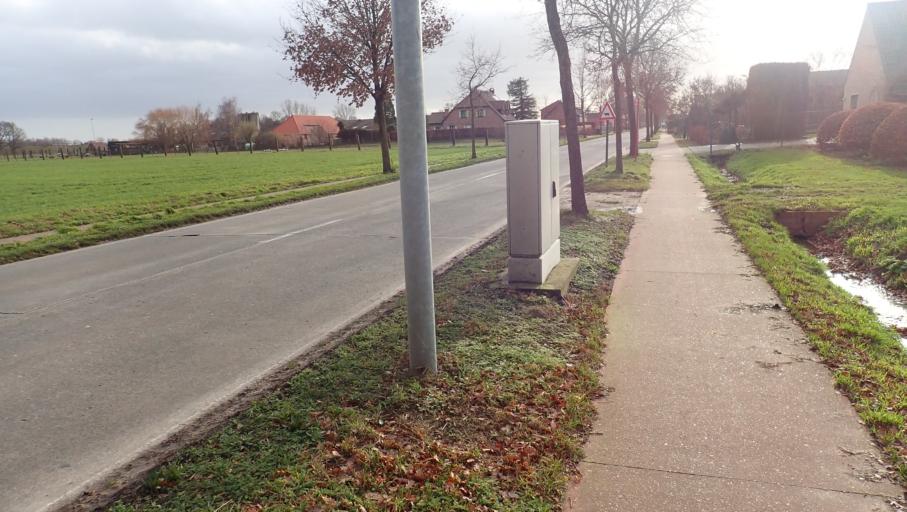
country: BE
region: Flanders
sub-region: Provincie Antwerpen
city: Brecht
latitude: 51.3736
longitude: 4.6443
